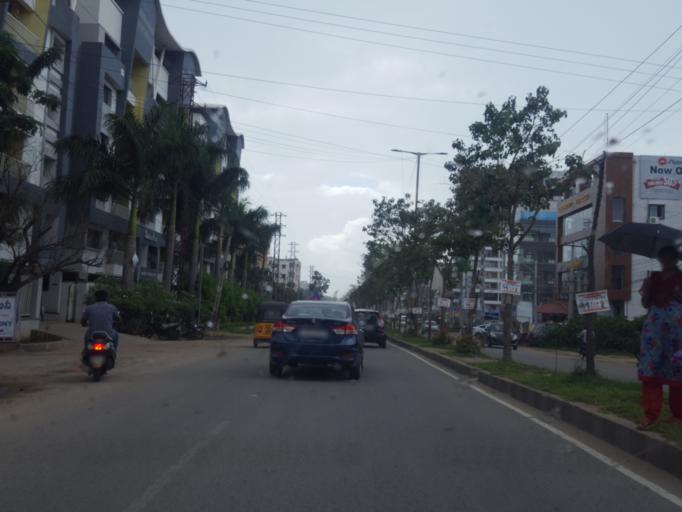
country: IN
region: Telangana
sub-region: Medak
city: Serilingampalle
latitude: 17.4799
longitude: 78.3175
